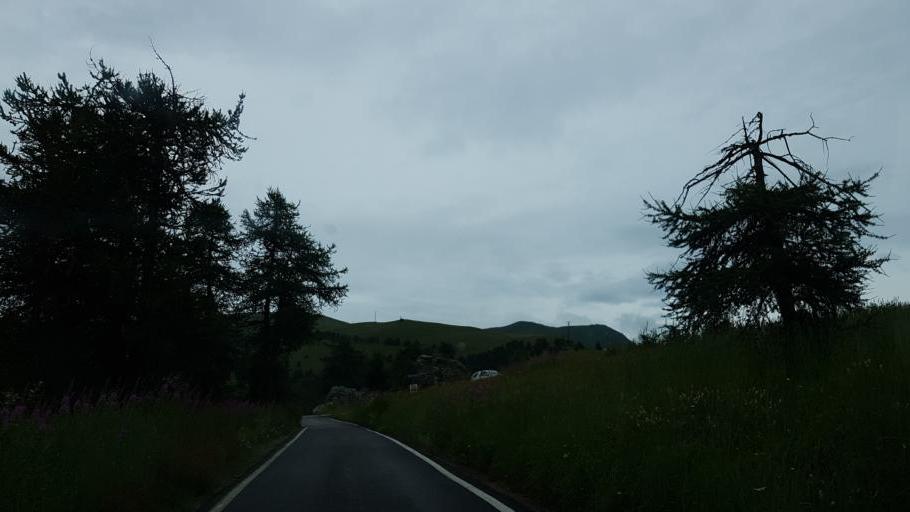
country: IT
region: Piedmont
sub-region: Provincia di Cuneo
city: Serre
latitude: 44.5264
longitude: 7.1033
